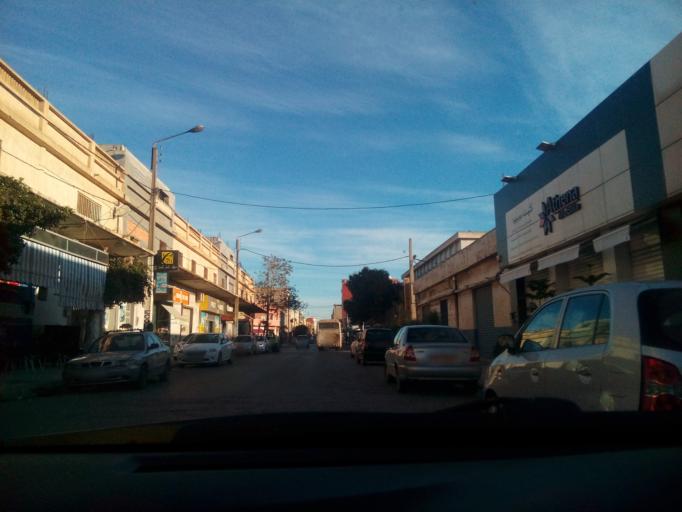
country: DZ
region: Oran
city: Oran
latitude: 35.6811
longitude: -0.6593
